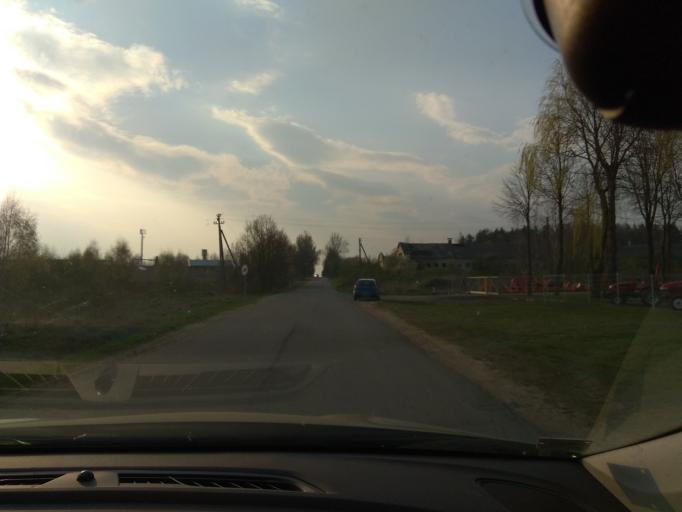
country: LT
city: Baltoji Voke
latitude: 54.5965
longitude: 25.1476
